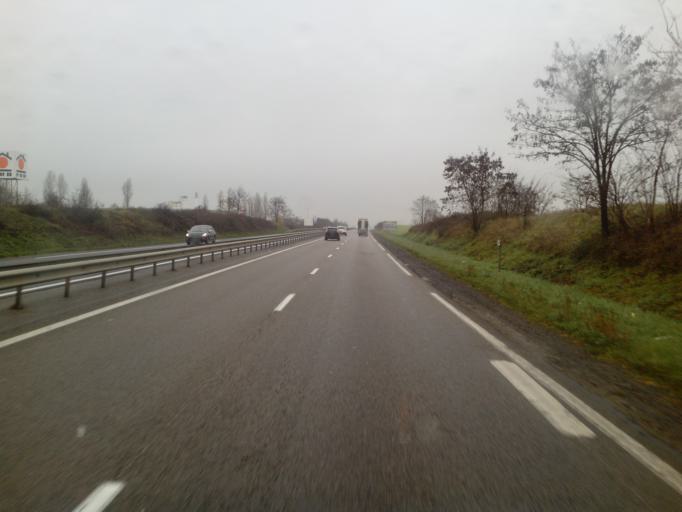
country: FR
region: Poitou-Charentes
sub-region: Departement de la Vienne
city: Montamise
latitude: 46.5880
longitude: 0.3918
